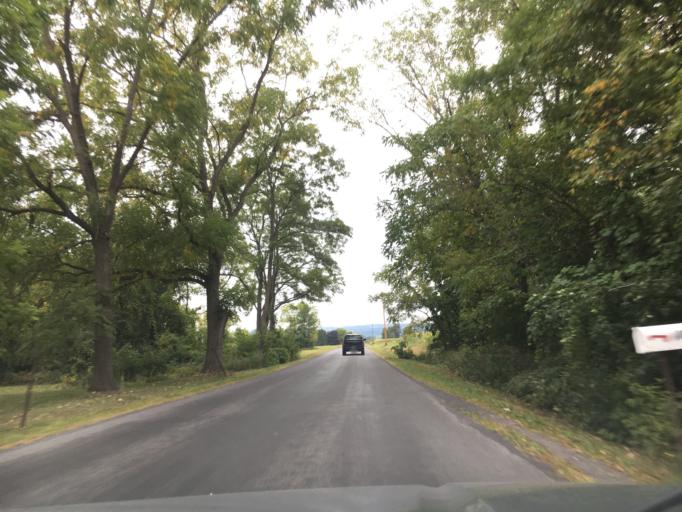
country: US
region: New York
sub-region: Tompkins County
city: Trumansburg
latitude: 42.6720
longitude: -76.7611
